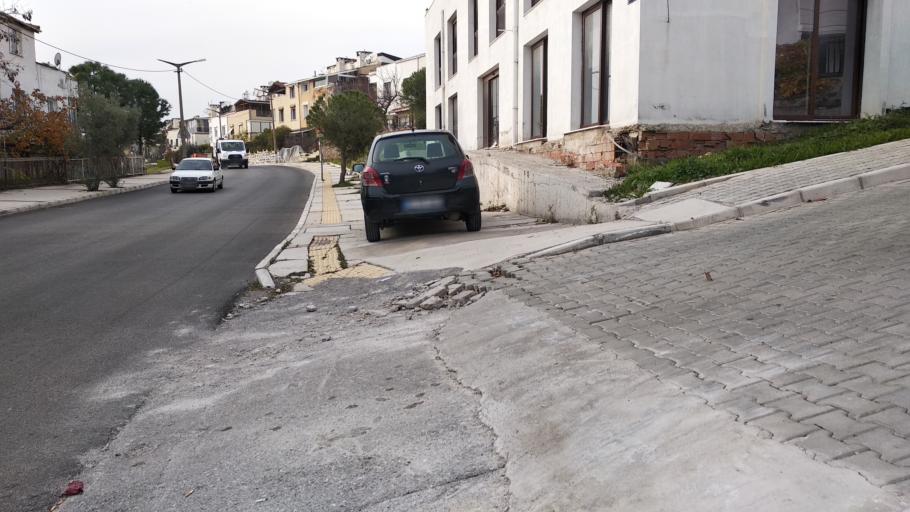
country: TR
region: Izmir
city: Karsiyaka
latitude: 38.4943
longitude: 27.0801
